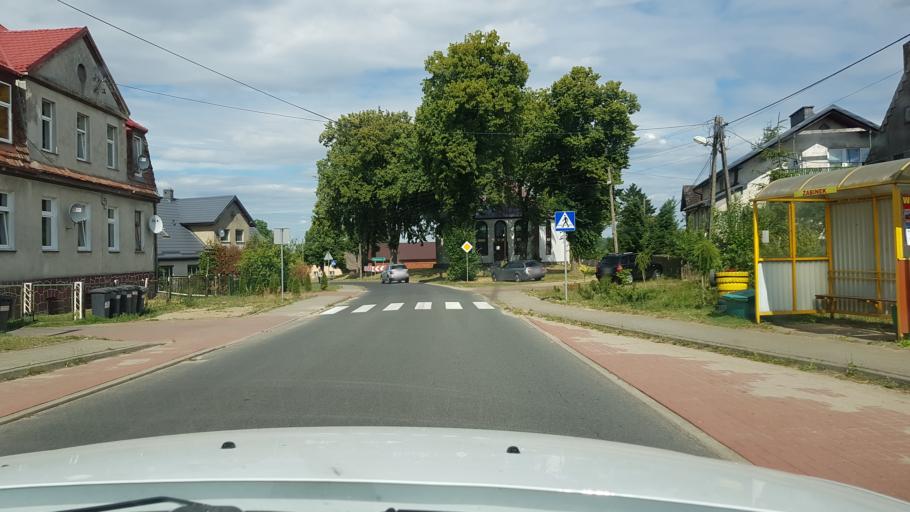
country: PL
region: West Pomeranian Voivodeship
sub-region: Powiat drawski
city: Wierzchowo
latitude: 53.4378
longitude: 16.0725
